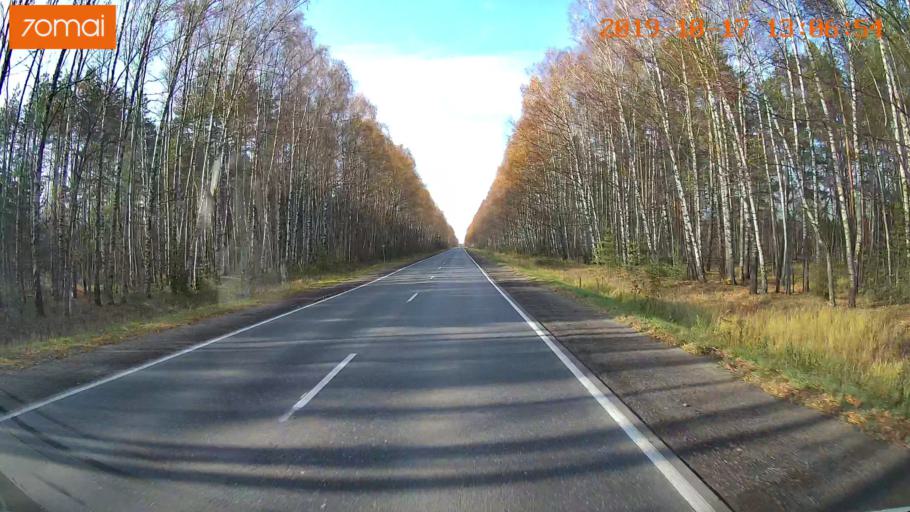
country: RU
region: Rjazan
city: Syntul
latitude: 54.9784
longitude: 41.3033
